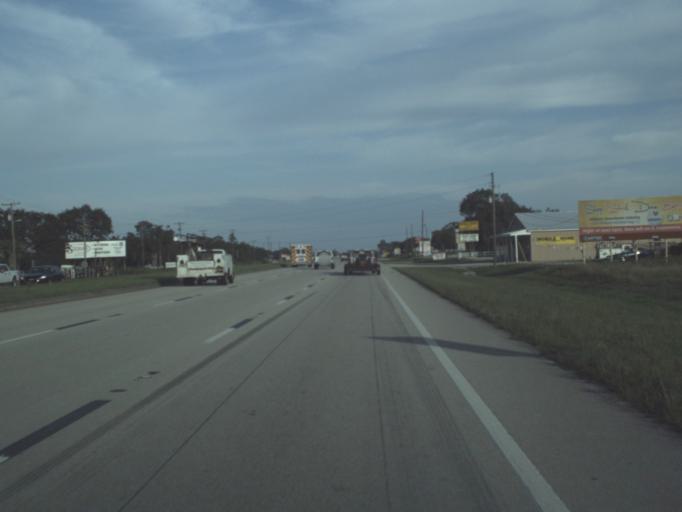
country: US
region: Florida
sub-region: Highlands County
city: Sebring
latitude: 27.4573
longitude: -81.4256
